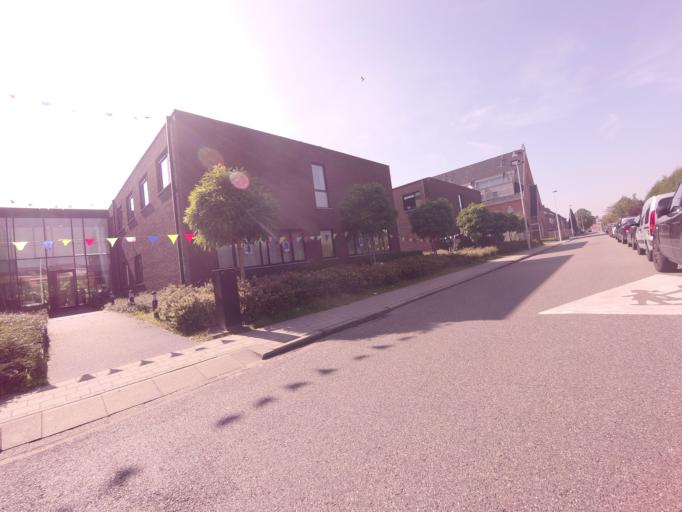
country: BE
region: Flanders
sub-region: Provincie Antwerpen
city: Boom
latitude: 51.0972
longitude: 4.3760
